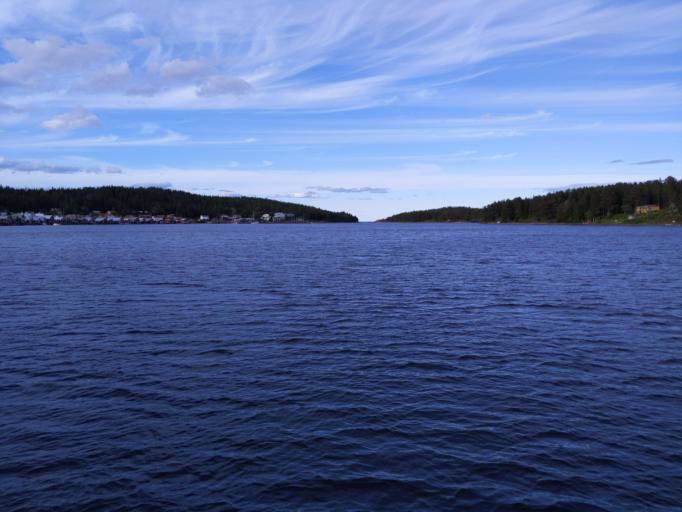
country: SE
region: Vaesternorrland
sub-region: OErnskoeldsviks Kommun
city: Kopmanholmen
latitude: 63.0170
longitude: 18.6446
